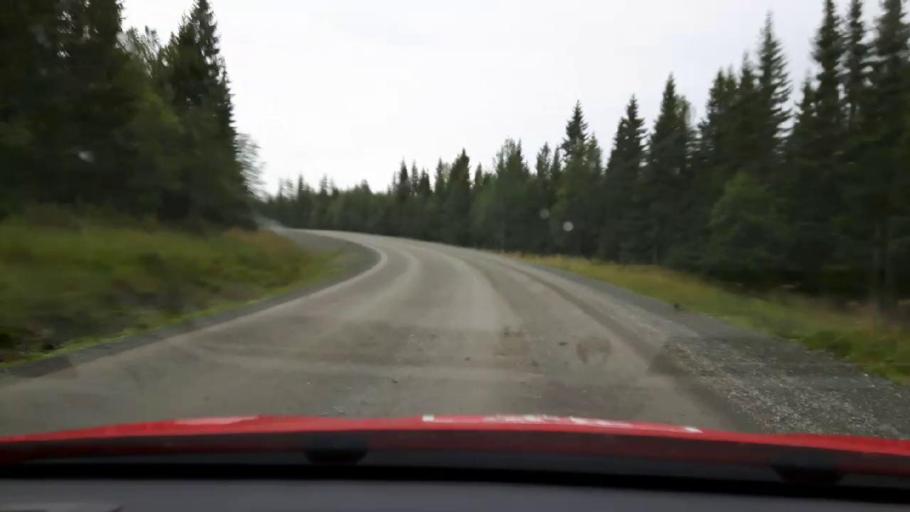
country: SE
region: Jaemtland
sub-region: Are Kommun
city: Are
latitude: 63.4502
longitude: 12.6554
